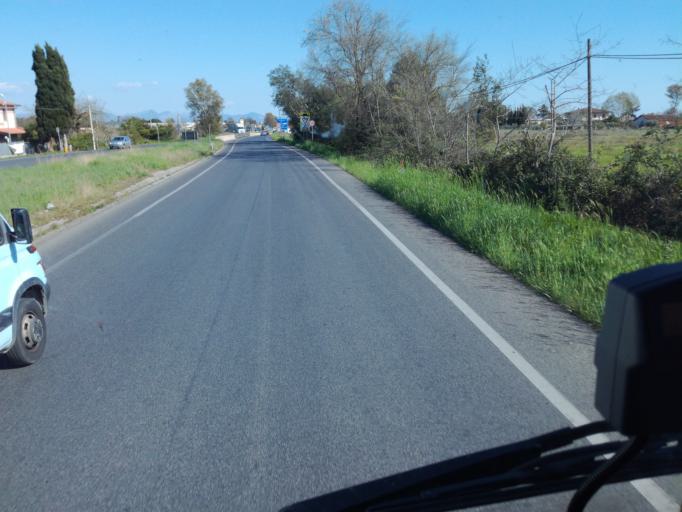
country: IT
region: Latium
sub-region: Provincia di Latina
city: Latina
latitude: 41.4356
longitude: 12.9278
